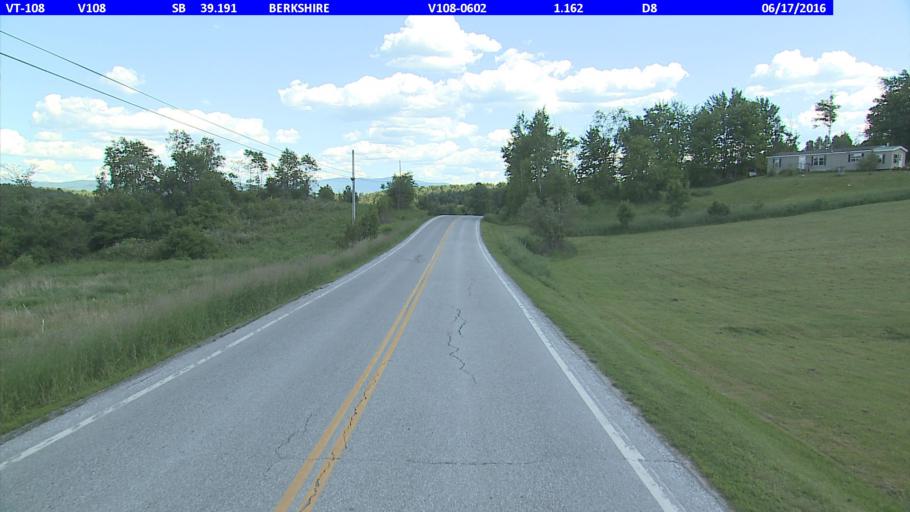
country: US
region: Vermont
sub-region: Franklin County
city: Enosburg Falls
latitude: 44.9414
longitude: -72.8134
